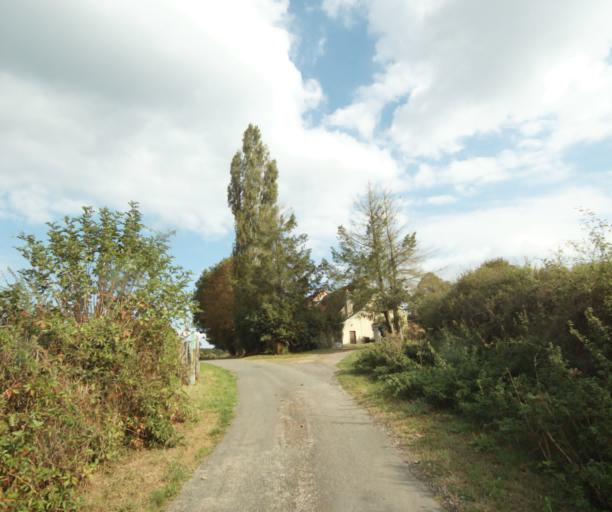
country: FR
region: Bourgogne
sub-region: Departement de Saone-et-Loire
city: Palinges
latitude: 46.5112
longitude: 4.2447
